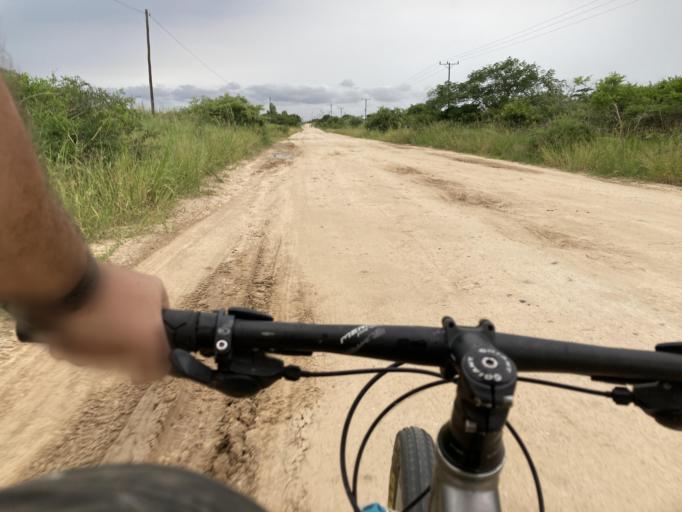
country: MZ
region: Maputo City
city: Maputo
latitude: -26.0513
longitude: 32.5326
